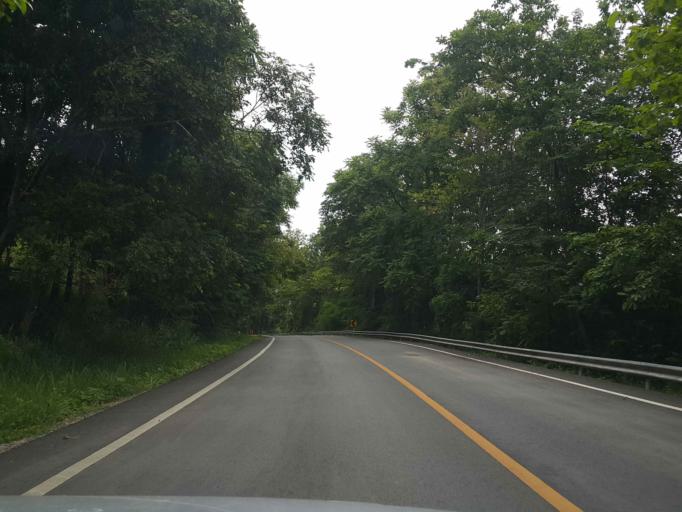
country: TH
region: Lampang
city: Thoen
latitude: 17.5517
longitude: 99.3384
